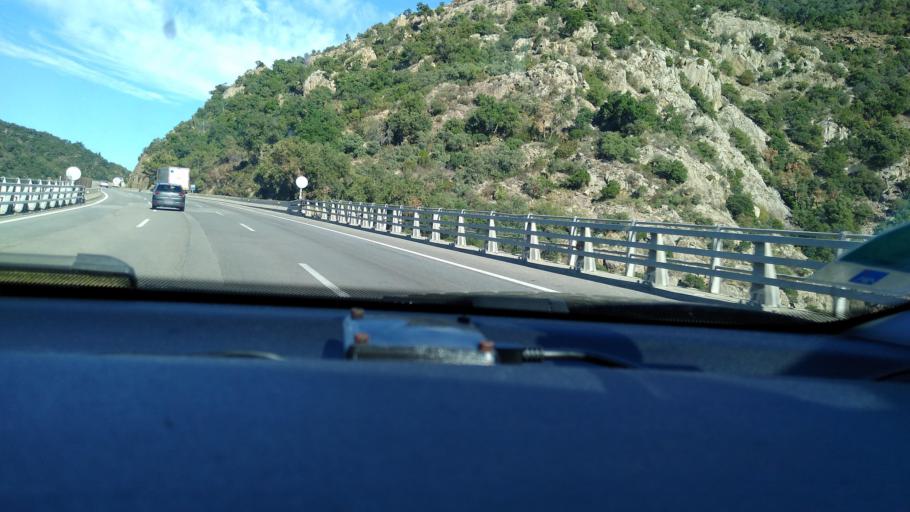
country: ES
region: Catalonia
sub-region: Provincia de Girona
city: la Jonquera
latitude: 42.4547
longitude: 2.8672
